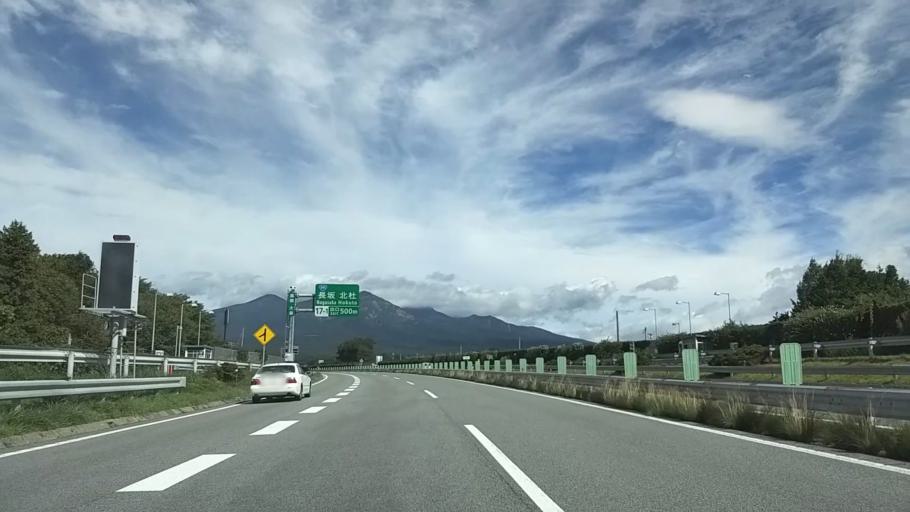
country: JP
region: Yamanashi
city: Nirasaki
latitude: 35.8306
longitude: 138.3925
